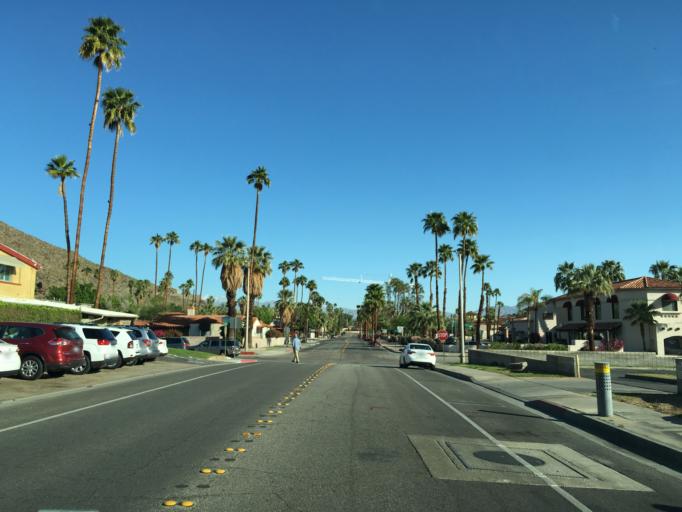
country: US
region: California
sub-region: Riverside County
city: Palm Springs
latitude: 33.8190
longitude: -116.5479
